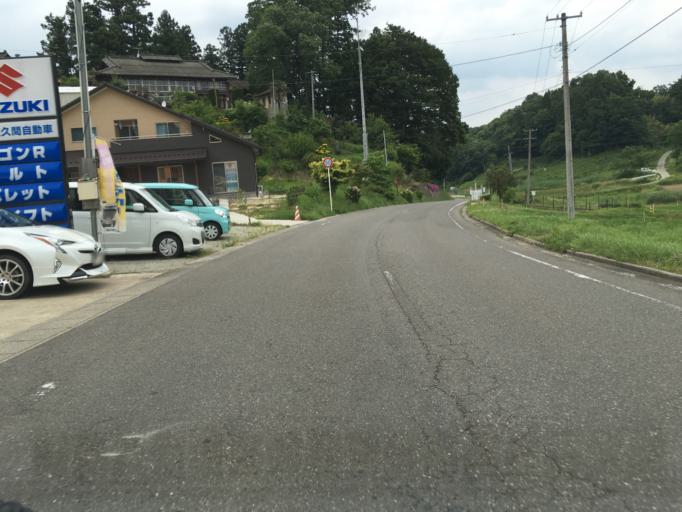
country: JP
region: Fukushima
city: Nihommatsu
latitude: 37.6316
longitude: 140.5385
